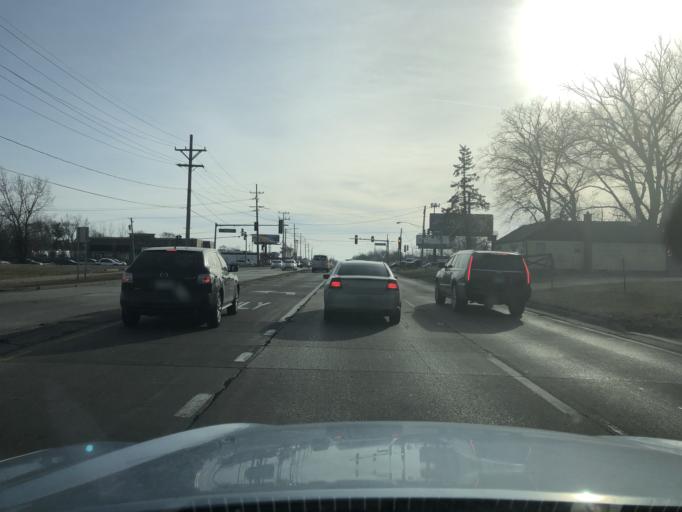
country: US
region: Illinois
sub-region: DuPage County
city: Roselle
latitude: 41.9990
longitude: -88.0802
